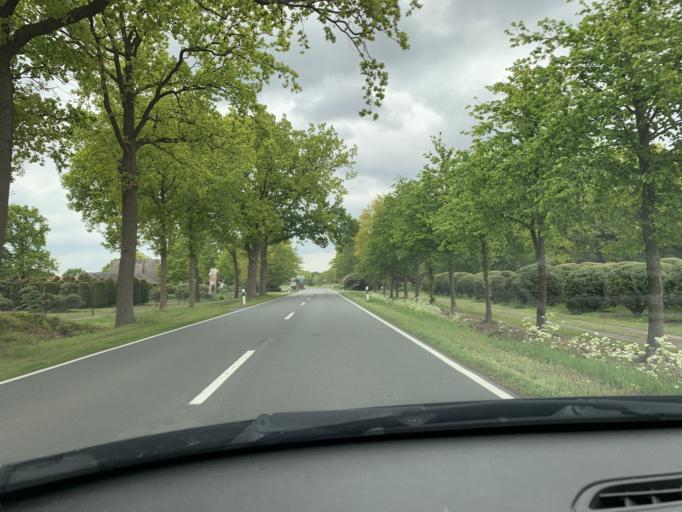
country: DE
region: Lower Saxony
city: Bad Zwischenahn
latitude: 53.1875
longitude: 8.0604
